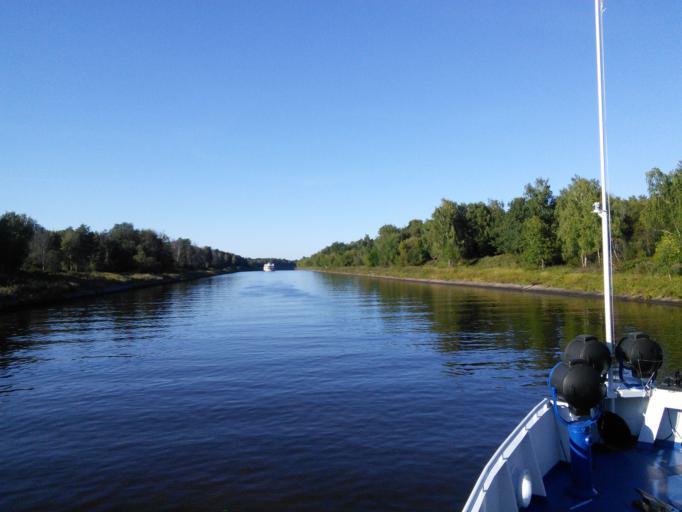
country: RU
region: Moskovskaya
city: Yakhroma
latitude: 56.3052
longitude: 37.4892
